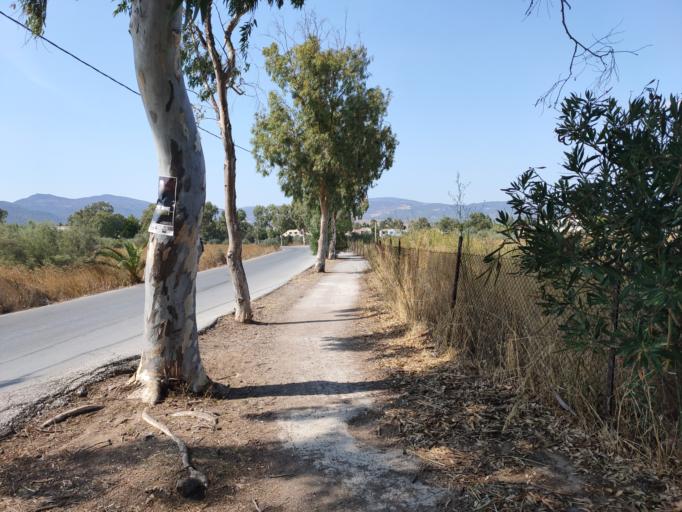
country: GR
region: North Aegean
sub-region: Nomos Lesvou
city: Kalloni
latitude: 39.2083
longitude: 26.2087
